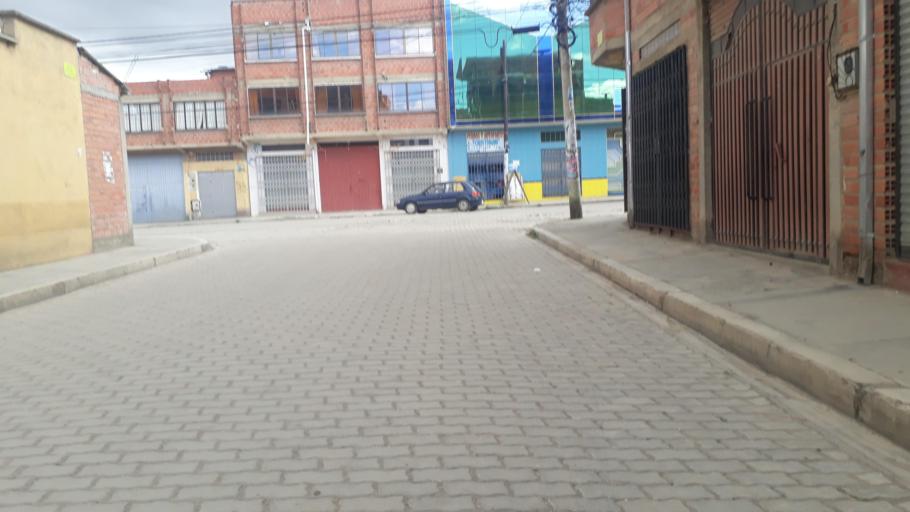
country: BO
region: La Paz
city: La Paz
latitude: -16.4935
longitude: -68.2147
